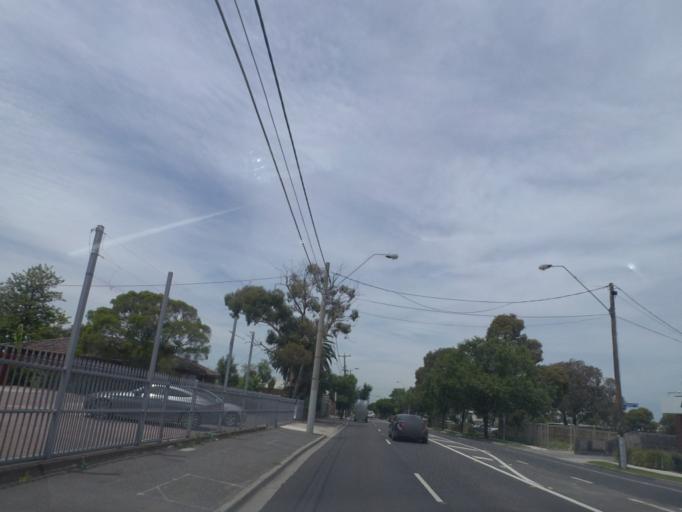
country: AU
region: Victoria
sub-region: Maribyrnong
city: Maribyrnong
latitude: -37.7897
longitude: 144.8862
